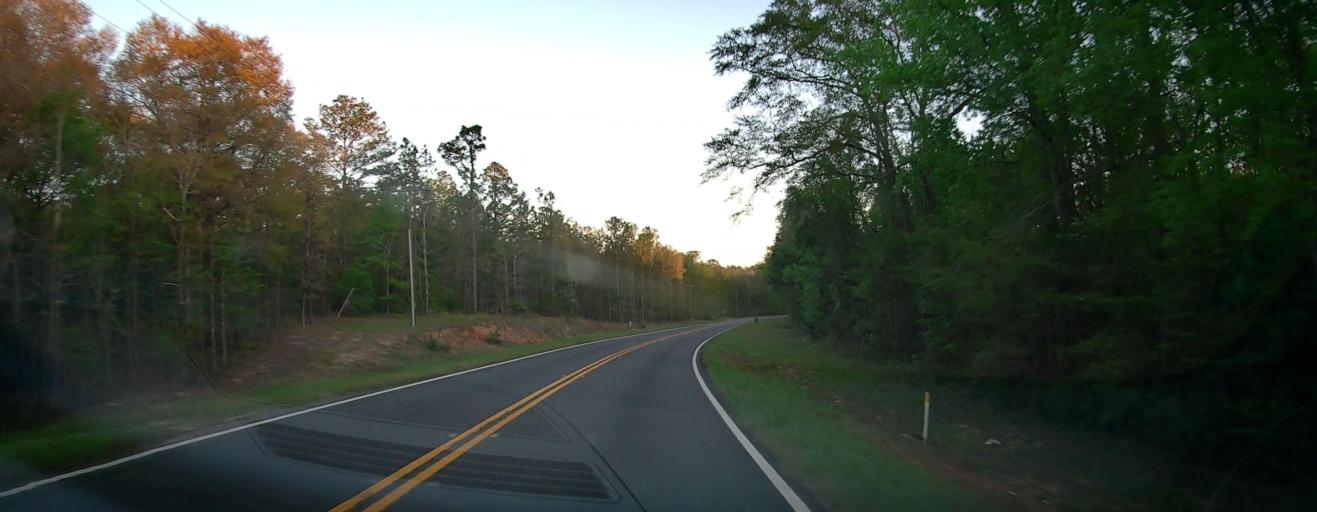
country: US
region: Georgia
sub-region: Marion County
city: Buena Vista
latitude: 32.4257
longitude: -84.5912
